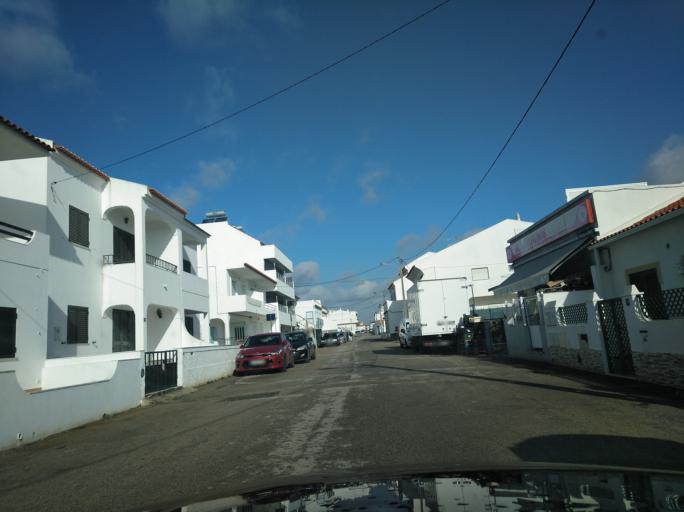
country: PT
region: Faro
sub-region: Vila Real de Santo Antonio
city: Monte Gordo
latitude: 37.1755
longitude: -7.4995
